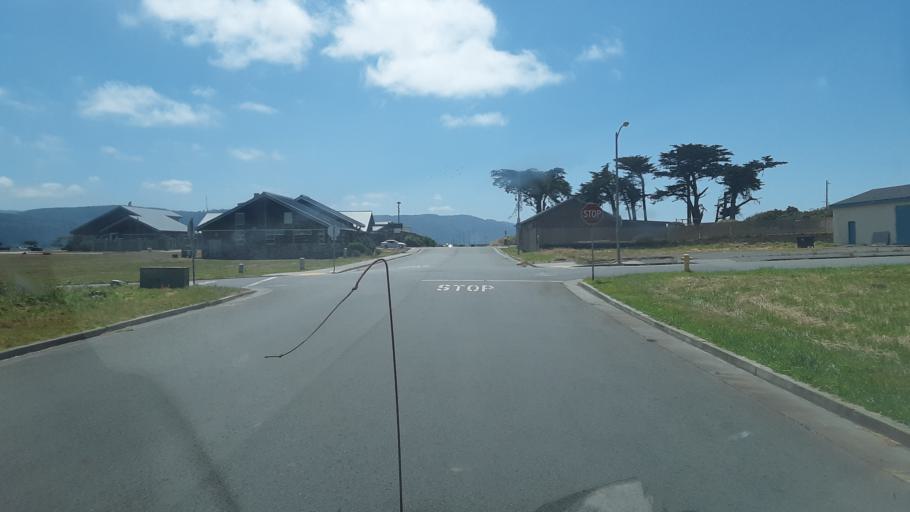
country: US
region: California
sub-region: Del Norte County
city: Crescent City
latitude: 41.7483
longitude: -124.2023
